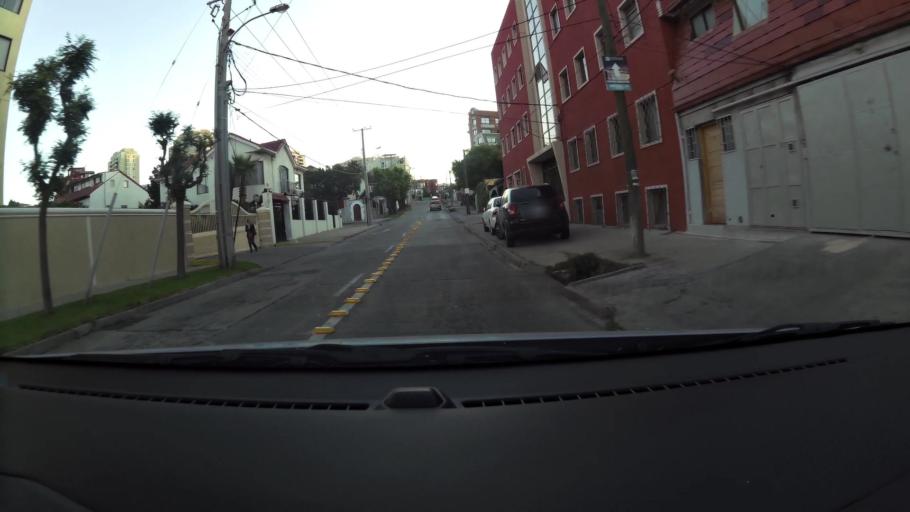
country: CL
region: Valparaiso
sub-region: Provincia de Valparaiso
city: Vina del Mar
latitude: -33.0254
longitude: -71.5706
